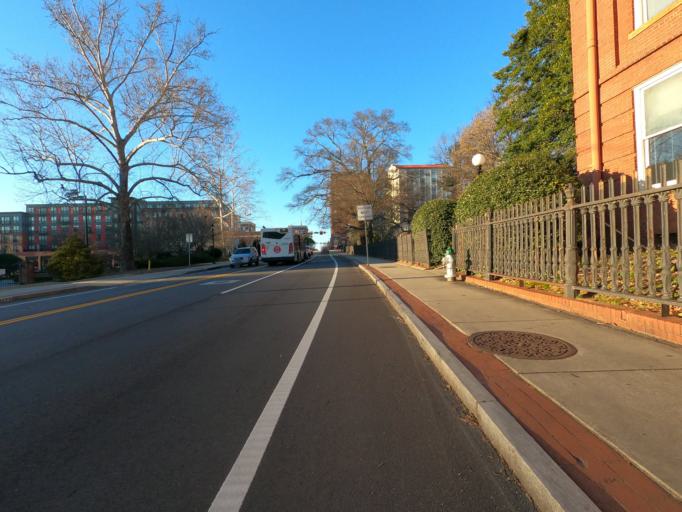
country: US
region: Georgia
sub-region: Clarke County
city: Athens
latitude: 33.9565
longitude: -83.3765
